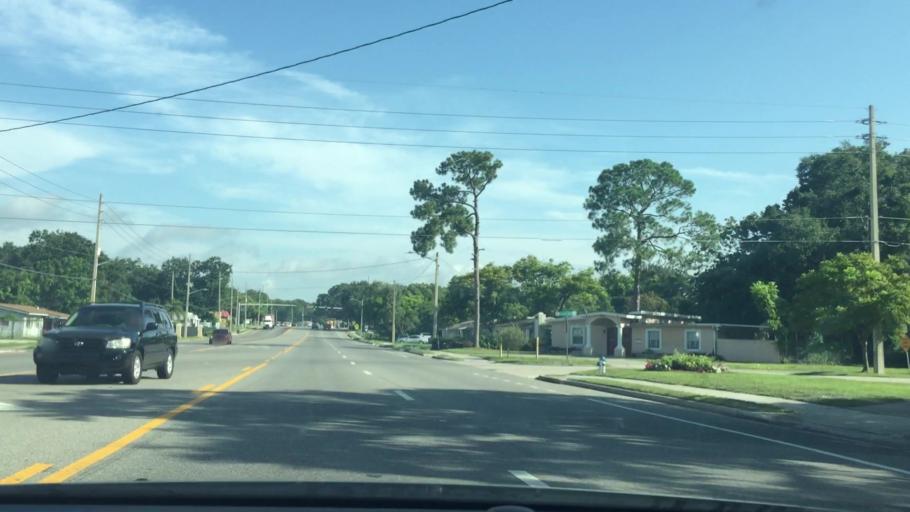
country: US
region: Florida
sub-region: Orange County
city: Pine Hills
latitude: 28.5560
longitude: -81.4477
